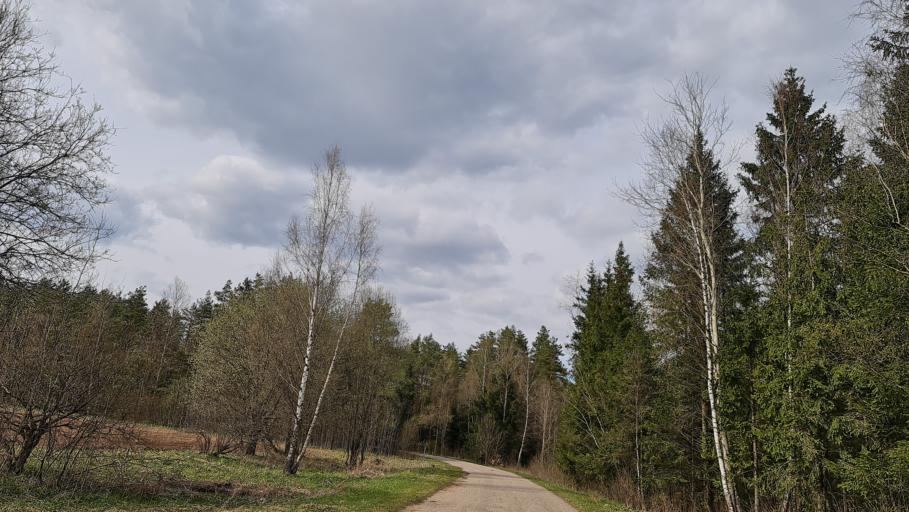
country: BY
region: Vitebsk
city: Byahoml'
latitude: 54.7479
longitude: 28.0411
